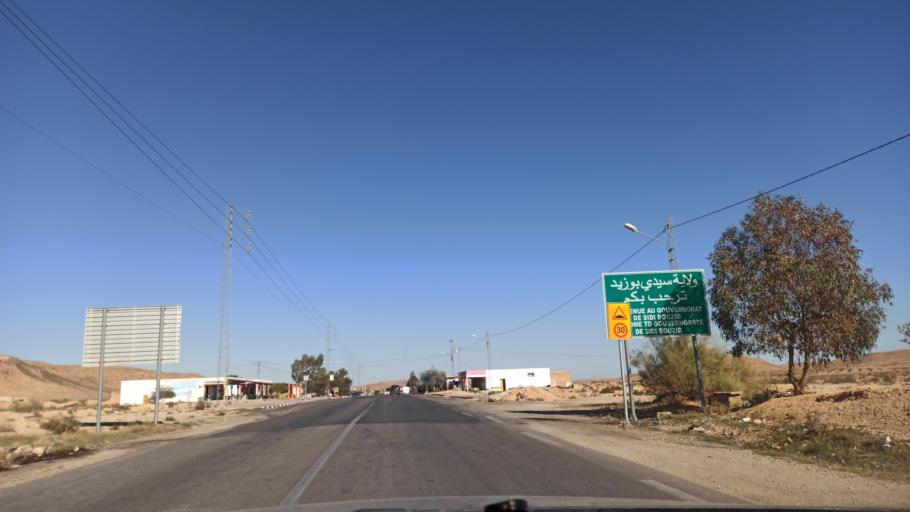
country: TN
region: Sidi Bu Zayd
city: Bi'r al Hufayy
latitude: 34.7029
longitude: 9.0442
